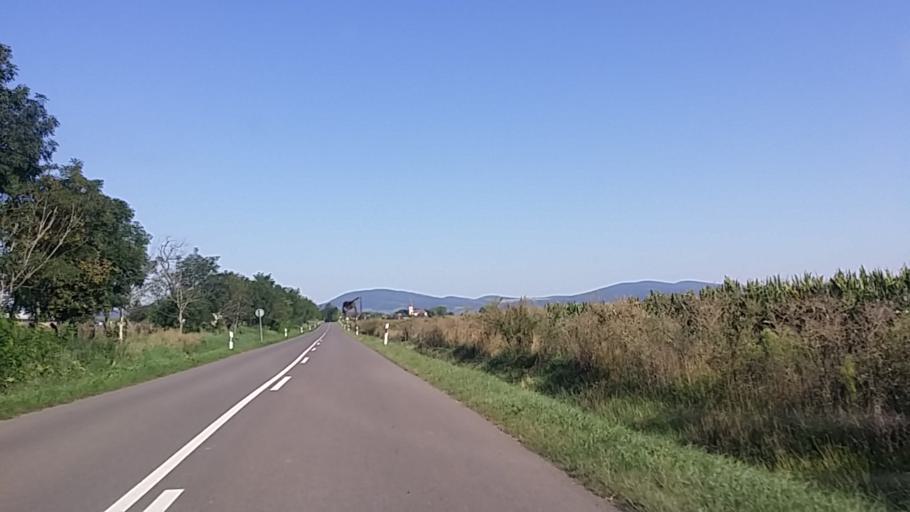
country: HU
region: Nograd
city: Jobbagyi
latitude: 47.8522
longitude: 19.6292
